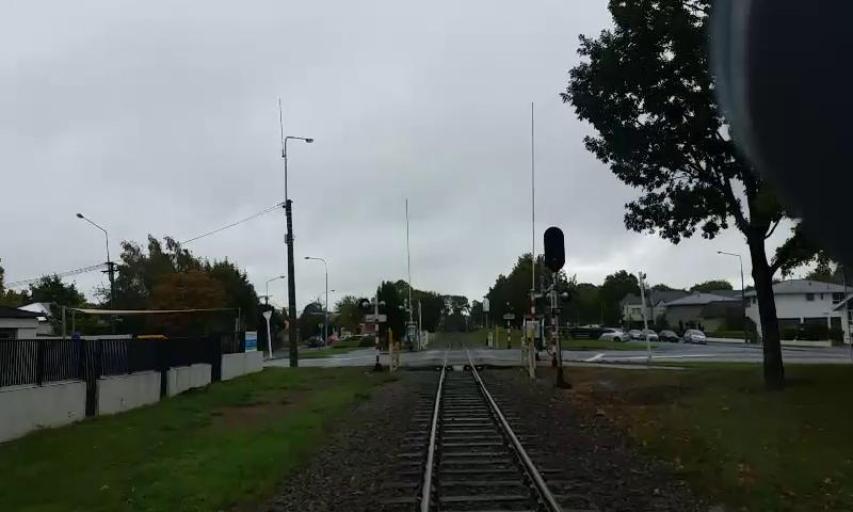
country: NZ
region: Canterbury
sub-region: Christchurch City
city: Christchurch
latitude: -43.5272
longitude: 172.6084
